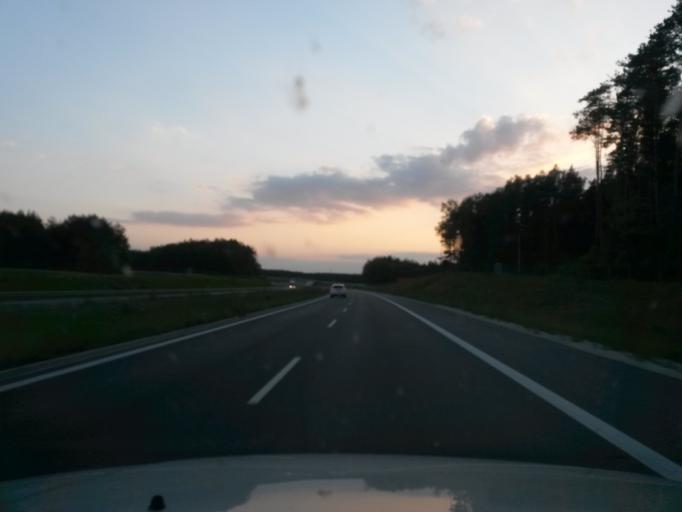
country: PL
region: Greater Poland Voivodeship
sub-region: Powiat kepinski
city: Perzow
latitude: 51.3039
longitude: 17.7891
